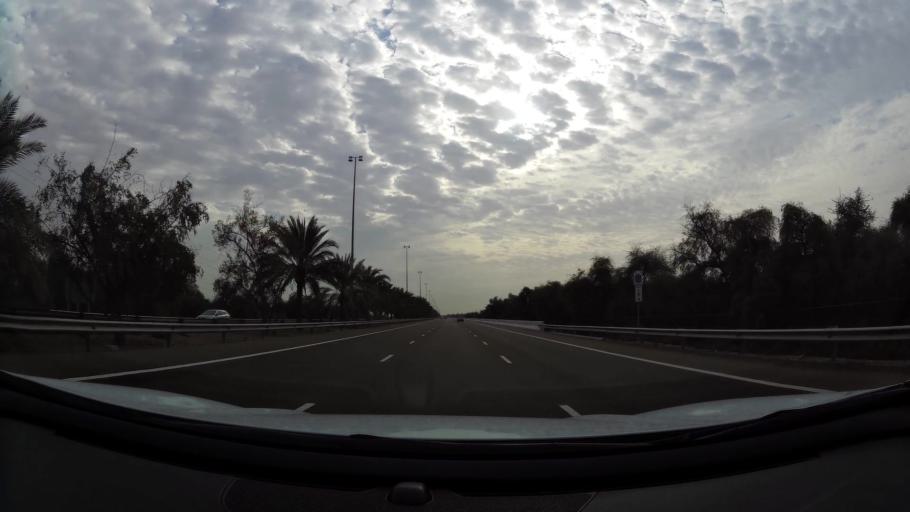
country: AE
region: Abu Dhabi
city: Al Ain
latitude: 24.1747
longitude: 55.2035
